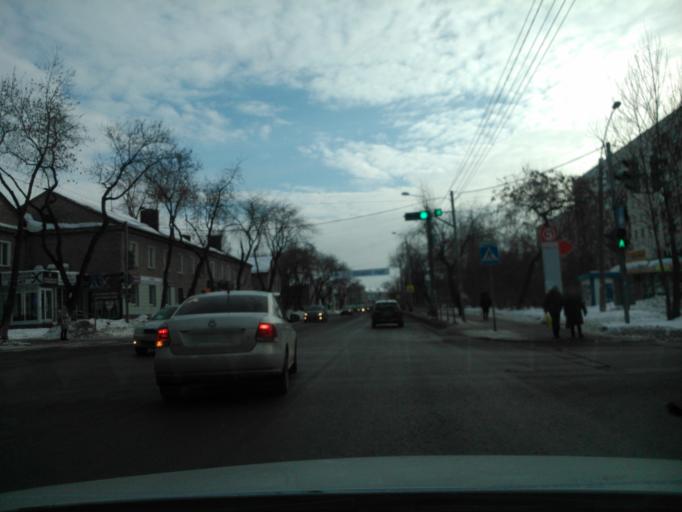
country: RU
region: Perm
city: Perm
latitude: 57.9962
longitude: 56.2450
